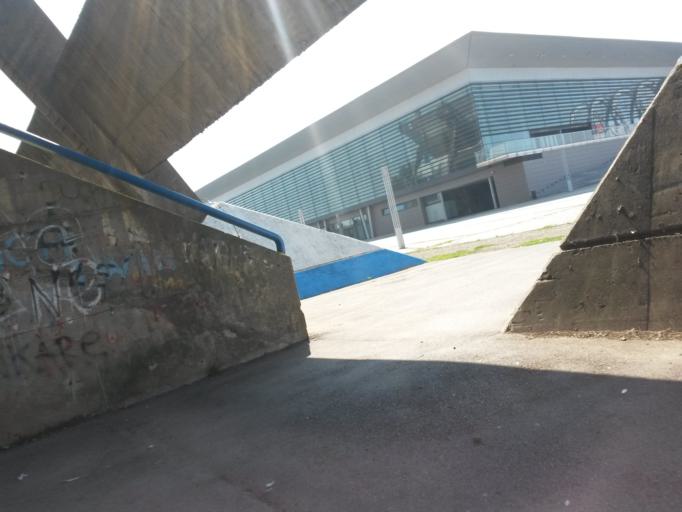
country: HR
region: Osjecko-Baranjska
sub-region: Grad Osijek
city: Osijek
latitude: 45.5451
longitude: 18.6944
